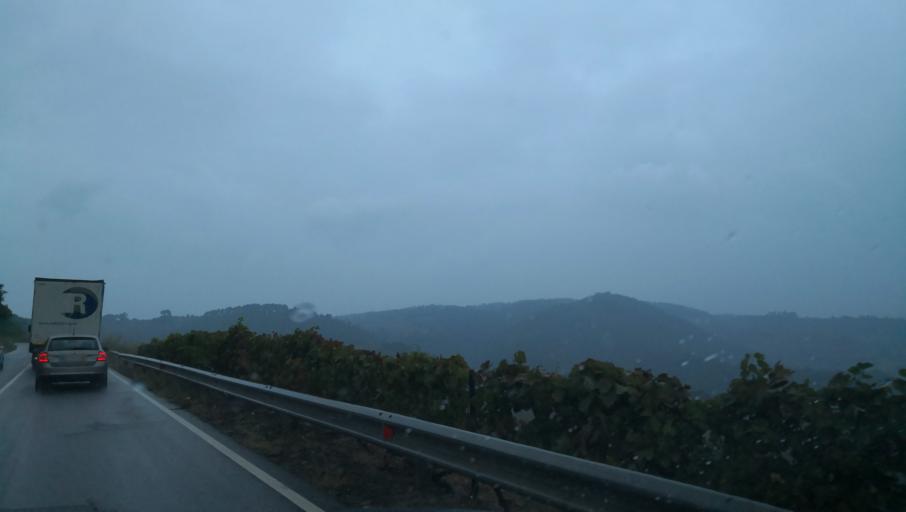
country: PT
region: Vila Real
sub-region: Vila Real
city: Vila Real
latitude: 41.2283
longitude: -7.7269
